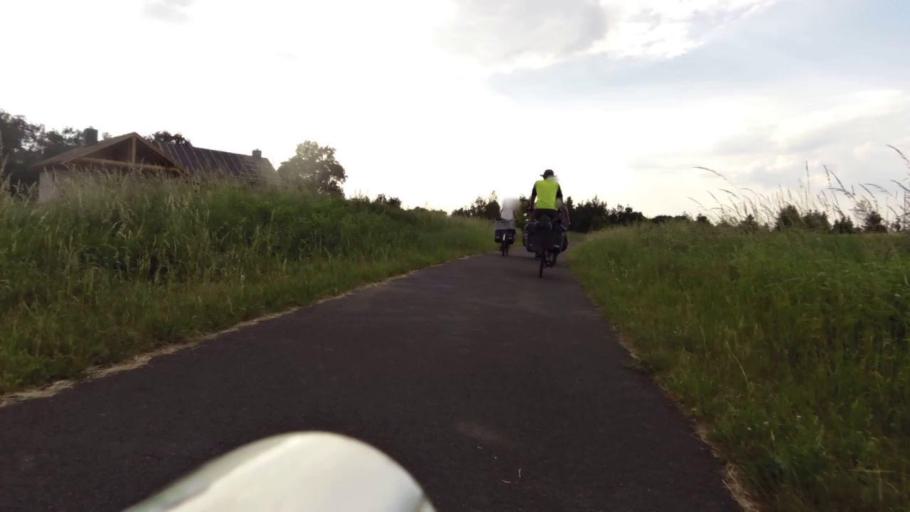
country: PL
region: Kujawsko-Pomorskie
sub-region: Powiat torunski
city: Lubianka
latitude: 53.1108
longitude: 18.4756
